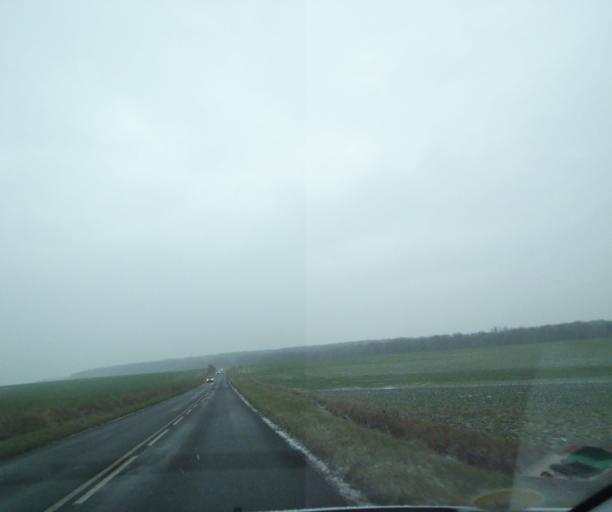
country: FR
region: Champagne-Ardenne
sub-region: Departement de la Haute-Marne
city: Wassy
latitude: 48.4797
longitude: 5.0044
